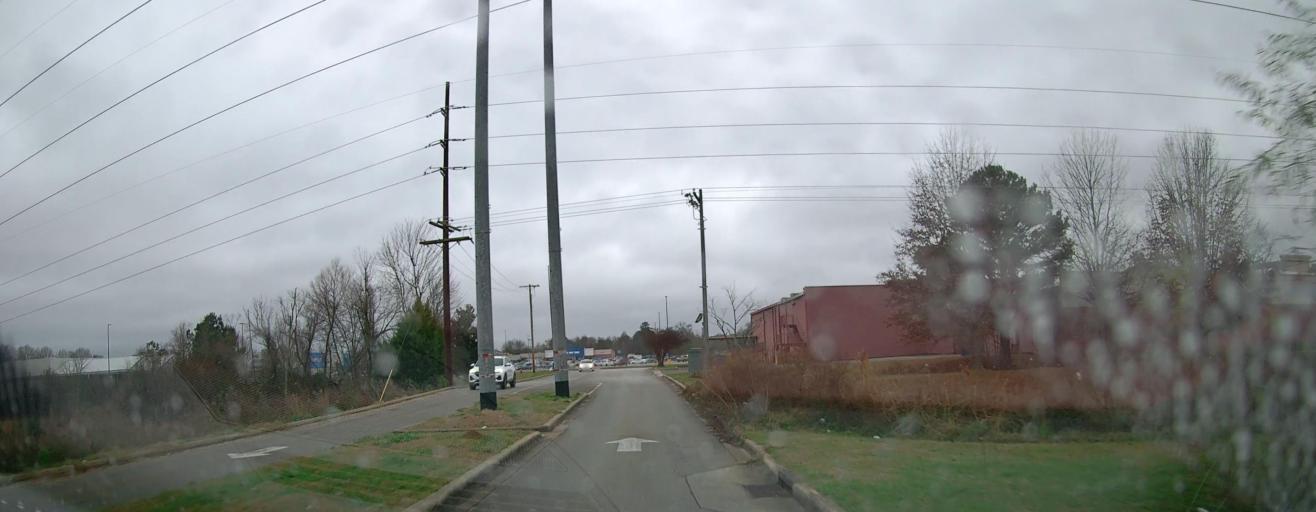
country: US
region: Alabama
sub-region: Morgan County
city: Flint City
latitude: 34.5586
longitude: -86.9978
